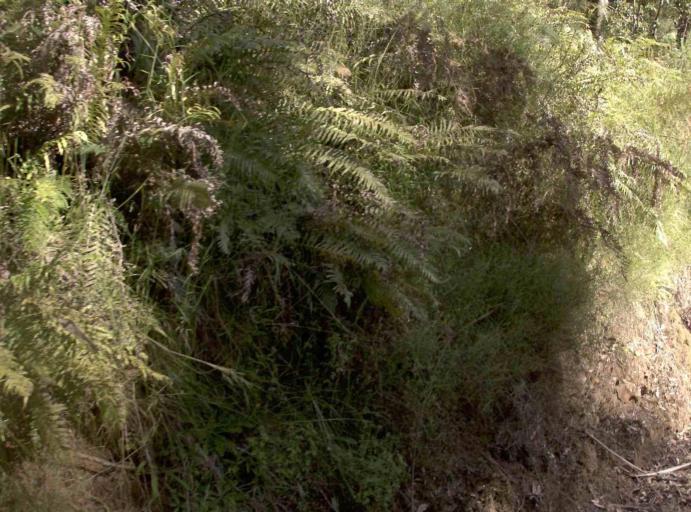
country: AU
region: Victoria
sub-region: East Gippsland
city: Lakes Entrance
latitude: -37.4067
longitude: 148.5929
